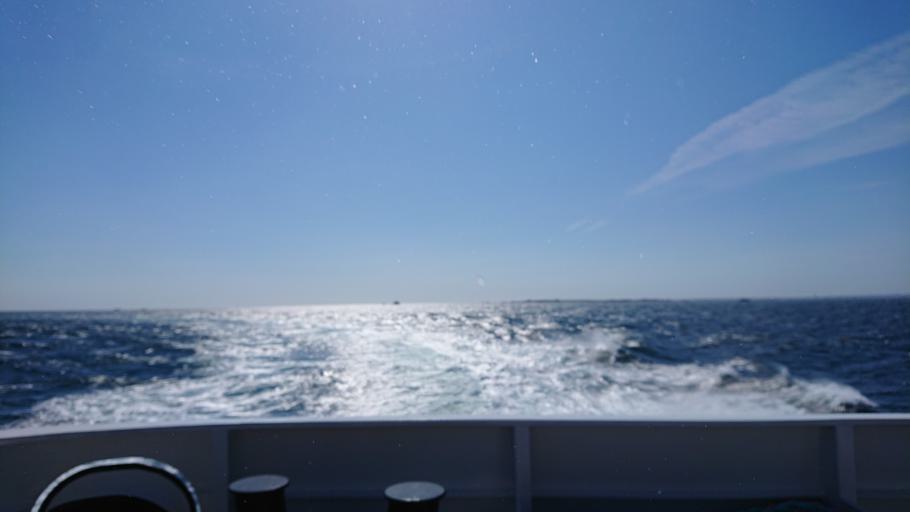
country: FR
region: Brittany
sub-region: Departement du Finistere
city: Le Conquet
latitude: 48.4156
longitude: -4.9449
